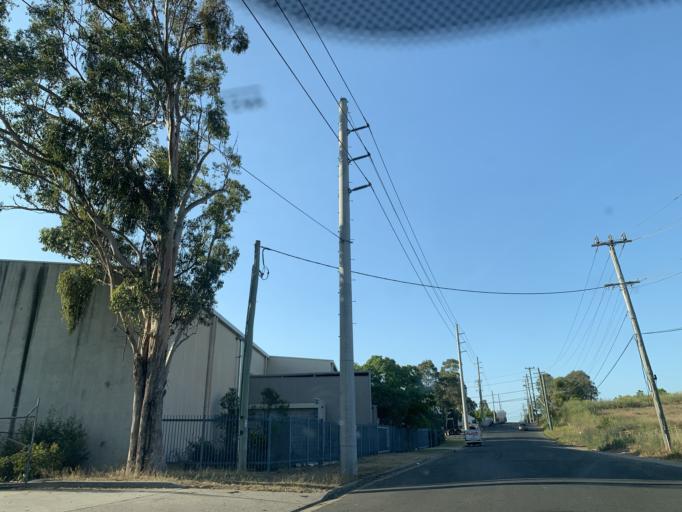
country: AU
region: New South Wales
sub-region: Fairfield
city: Horsley Park
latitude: -33.8366
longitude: 150.8819
